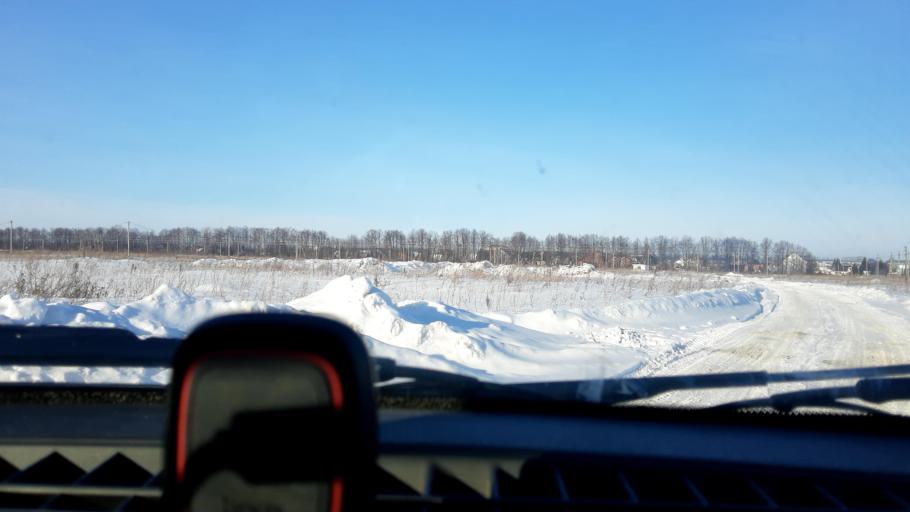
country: RU
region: Bashkortostan
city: Avdon
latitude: 54.4885
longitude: 55.8782
